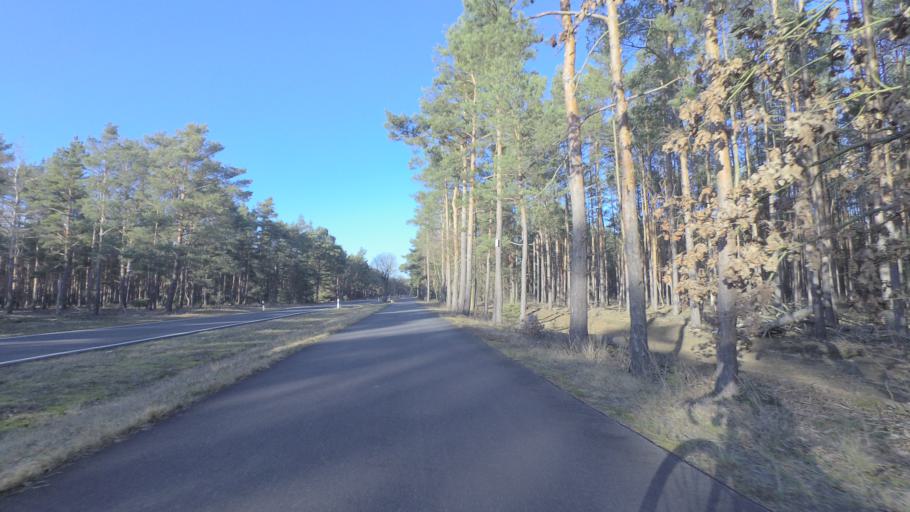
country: DE
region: Brandenburg
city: Sperenberg
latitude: 52.0297
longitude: 13.3185
